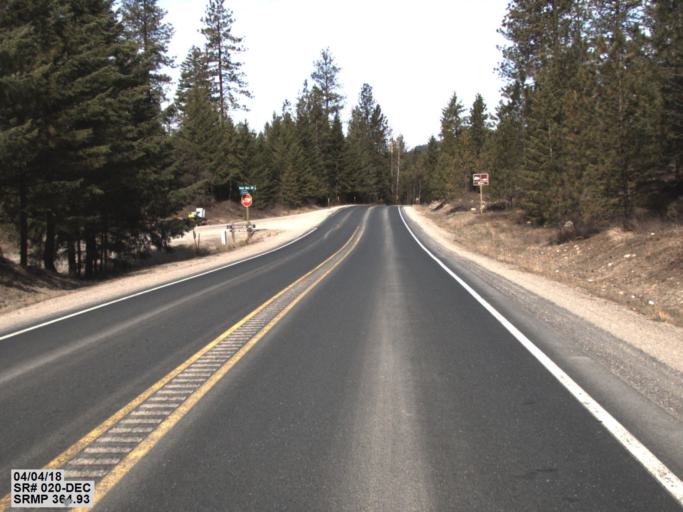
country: US
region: Washington
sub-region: Stevens County
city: Colville
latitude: 48.5036
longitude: -117.7163
